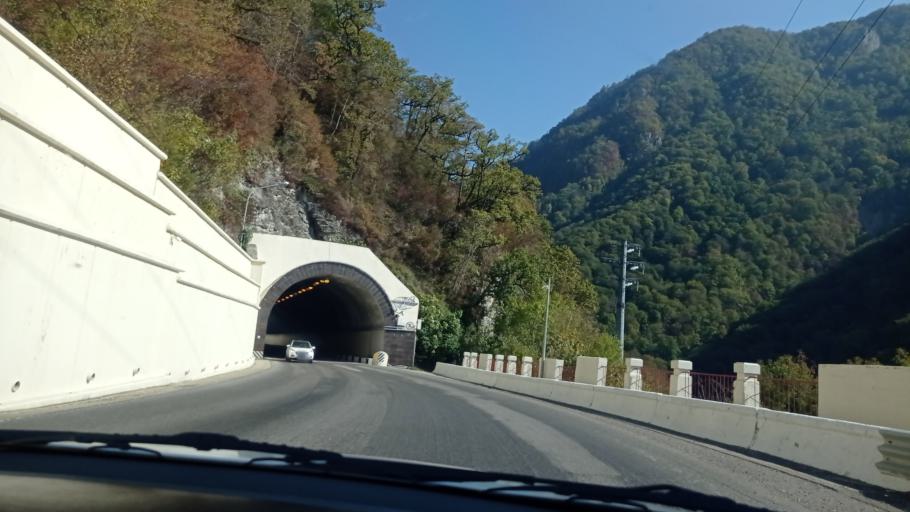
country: RU
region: Krasnodarskiy
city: Vysokoye
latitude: 43.5937
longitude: 40.0159
